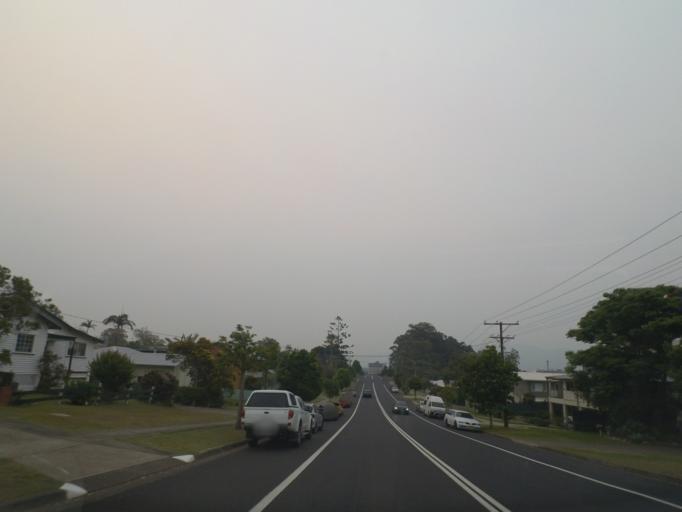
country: AU
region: New South Wales
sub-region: Coffs Harbour
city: Coffs Harbour
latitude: -30.3034
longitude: 153.1196
